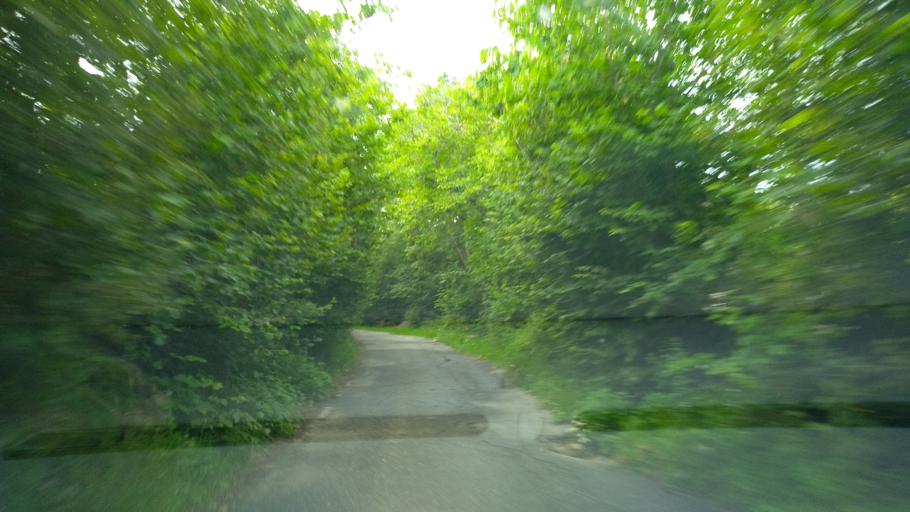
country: RO
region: Hunedoara
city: Salasu de Sus
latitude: 45.4748
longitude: 22.9613
